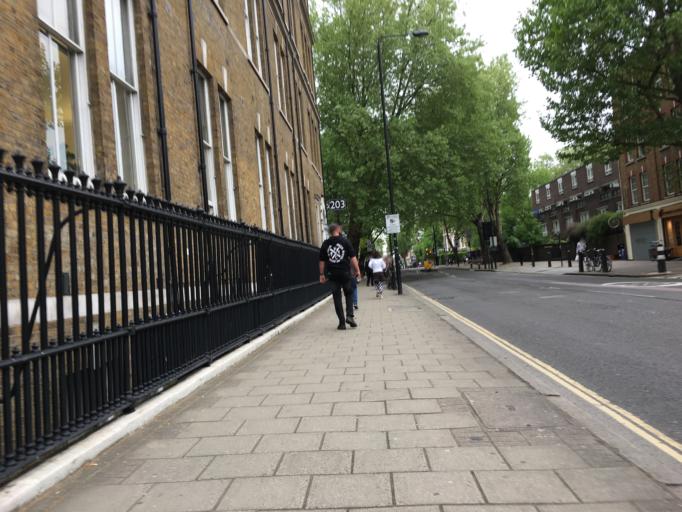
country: GB
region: England
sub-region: Greater London
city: Camden Town
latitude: 51.5323
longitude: -0.1362
